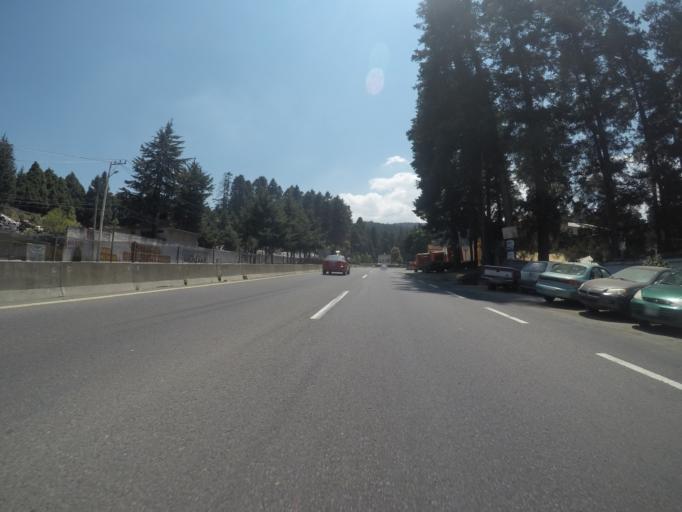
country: MX
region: Mexico City
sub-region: Cuajimalpa de Morelos
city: San Lorenzo Acopilco
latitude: 19.3113
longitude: -99.3321
